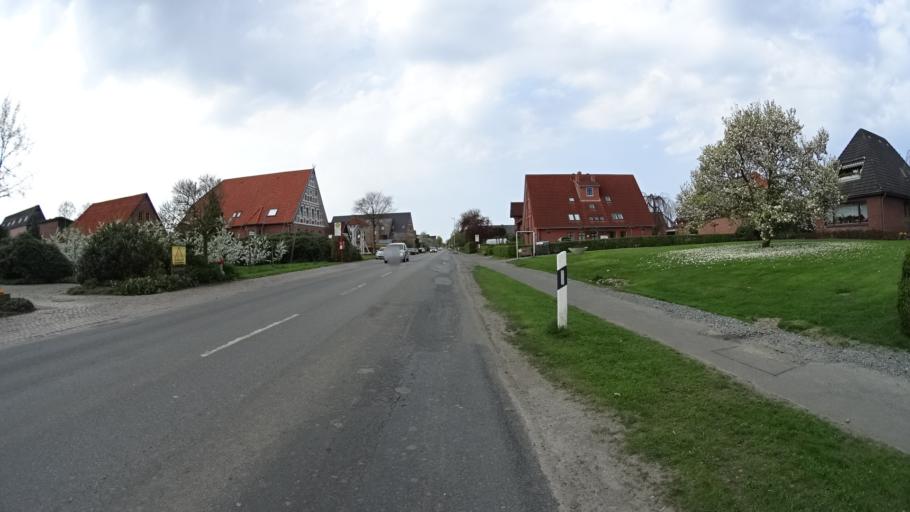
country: DE
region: Lower Saxony
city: Jork
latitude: 53.5296
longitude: 9.6949
